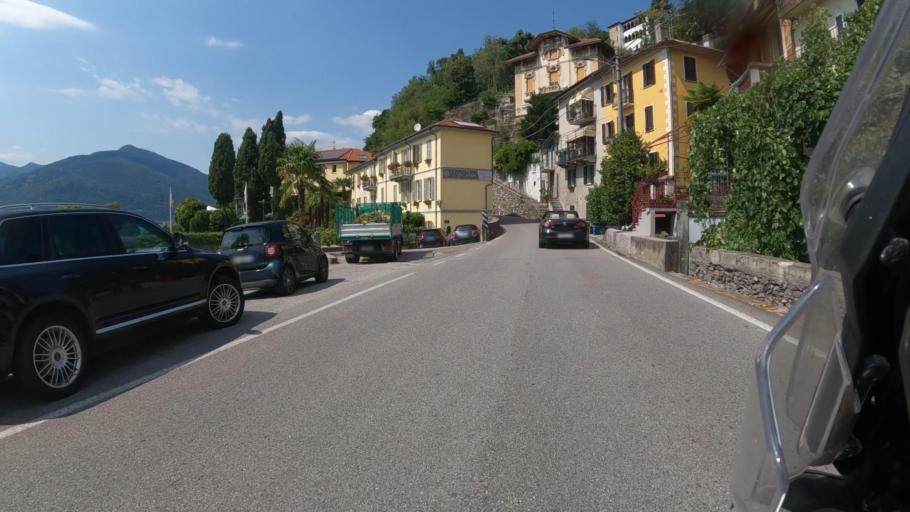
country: IT
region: Lombardy
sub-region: Provincia di Varese
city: Agra
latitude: 46.0251
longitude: 8.7513
